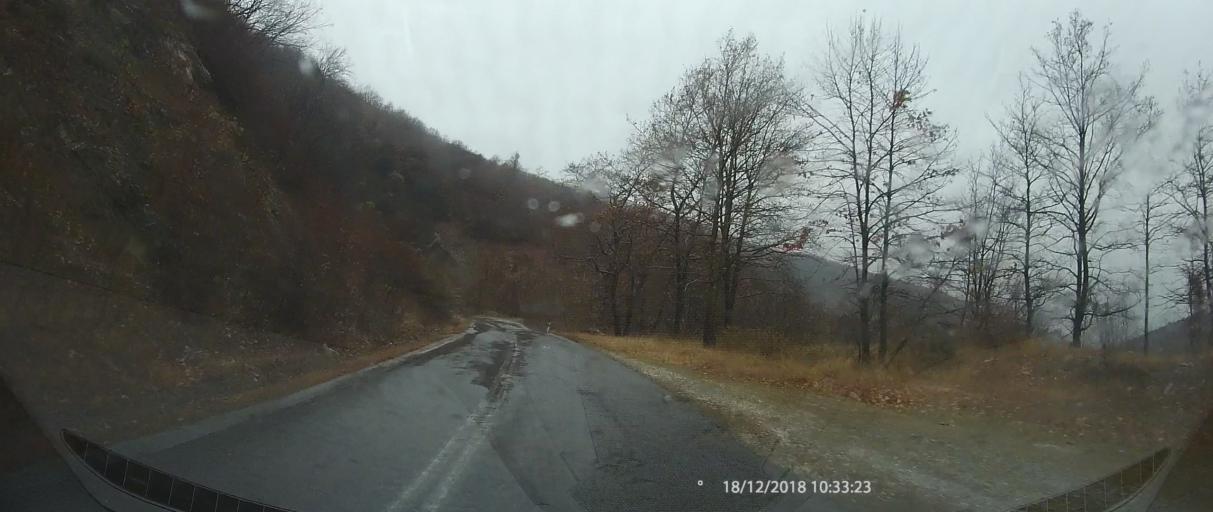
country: GR
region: Central Macedonia
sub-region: Nomos Pierias
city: Kato Milia
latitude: 40.1976
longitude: 22.3010
